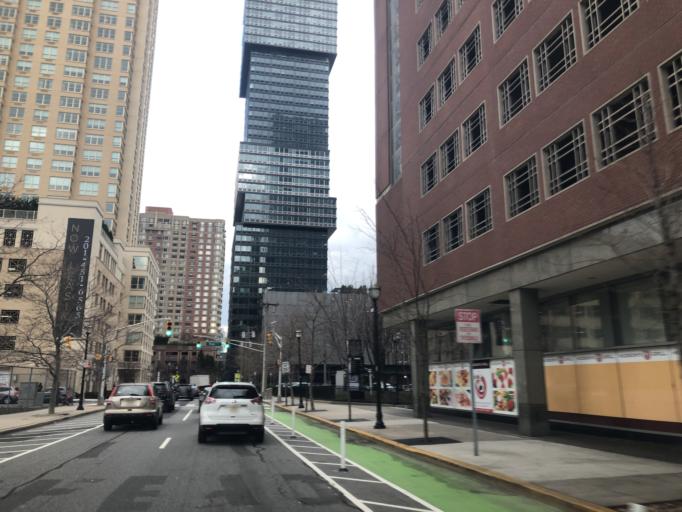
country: US
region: New Jersey
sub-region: Hudson County
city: Hoboken
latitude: 40.7188
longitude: -74.0353
